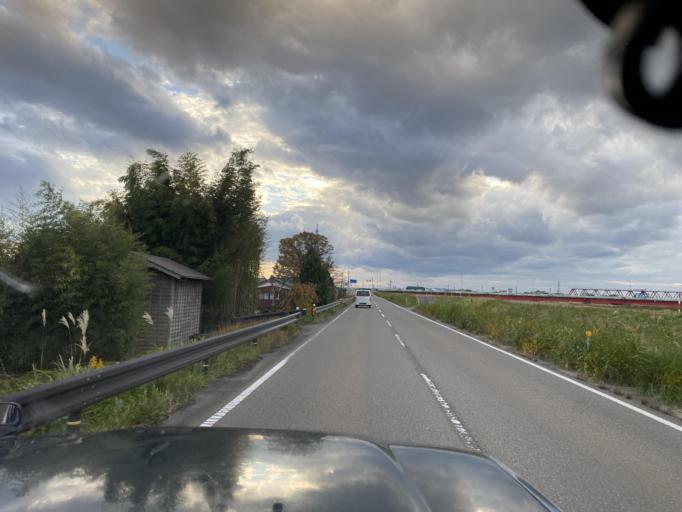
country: JP
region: Niigata
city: Sanjo
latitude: 37.6458
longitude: 138.9522
